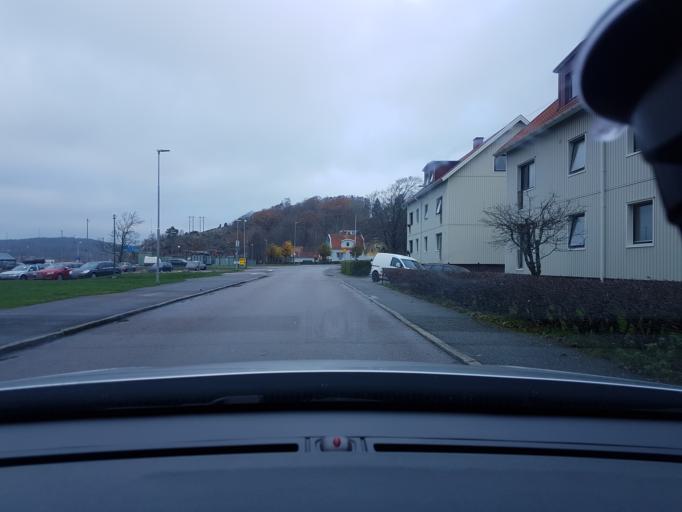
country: SE
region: Vaestra Goetaland
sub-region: Ale Kommun
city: Surte
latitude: 57.8512
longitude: 12.0176
